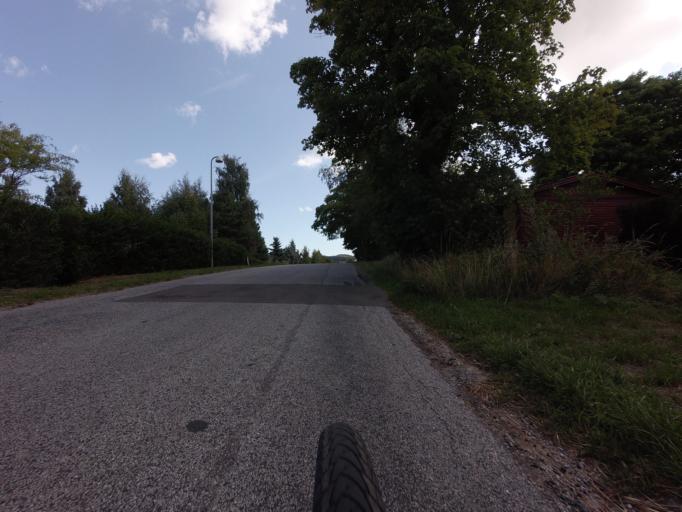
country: DK
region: Zealand
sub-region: Vordingborg Kommune
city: Stege
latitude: 54.9698
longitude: 12.4673
